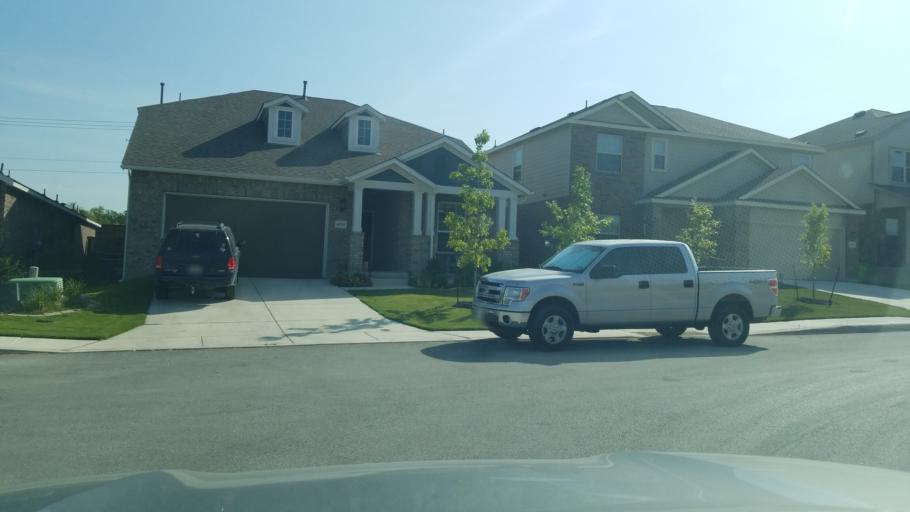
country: US
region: Texas
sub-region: Medina County
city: La Coste
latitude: 29.4069
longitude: -98.7849
